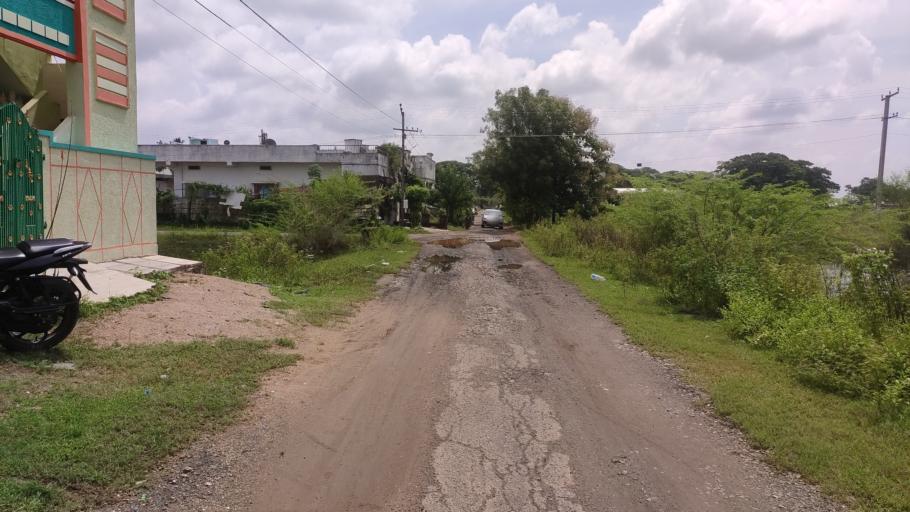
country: IN
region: Telangana
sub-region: Khammam
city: Khammam
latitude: 17.2439
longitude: 80.1936
